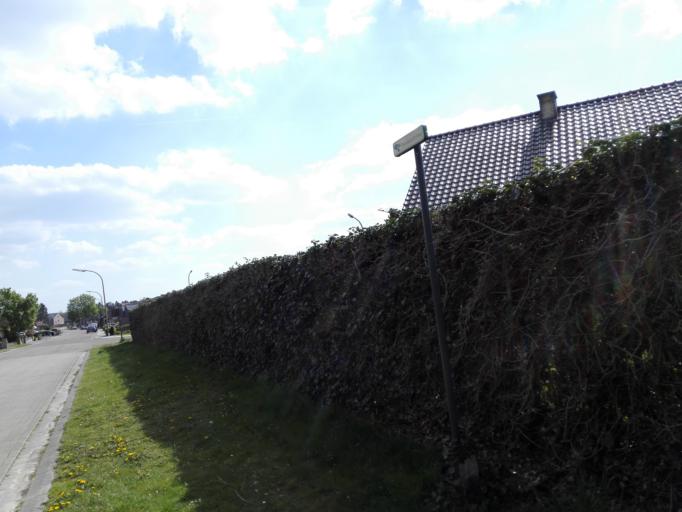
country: BE
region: Flanders
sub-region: Provincie Vlaams-Brabant
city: Rotselaar
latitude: 50.9522
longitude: 4.7225
